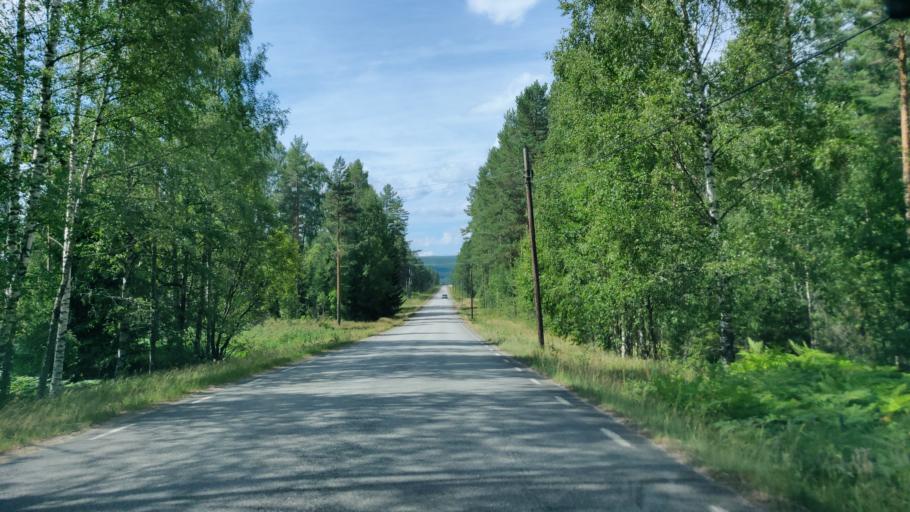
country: SE
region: Vaermland
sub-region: Hagfors Kommun
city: Ekshaerad
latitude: 60.0724
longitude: 13.5213
